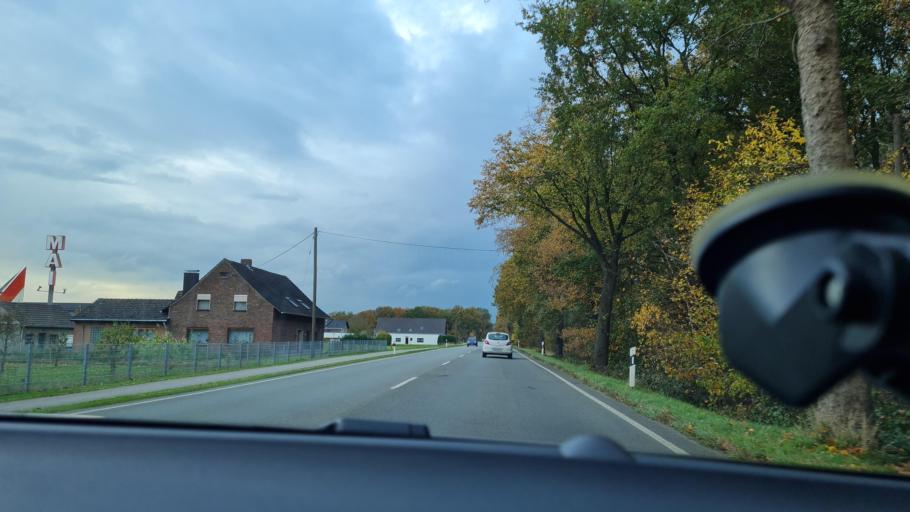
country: DE
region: North Rhine-Westphalia
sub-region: Regierungsbezirk Dusseldorf
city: Voerde
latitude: 51.6193
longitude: 6.6792
